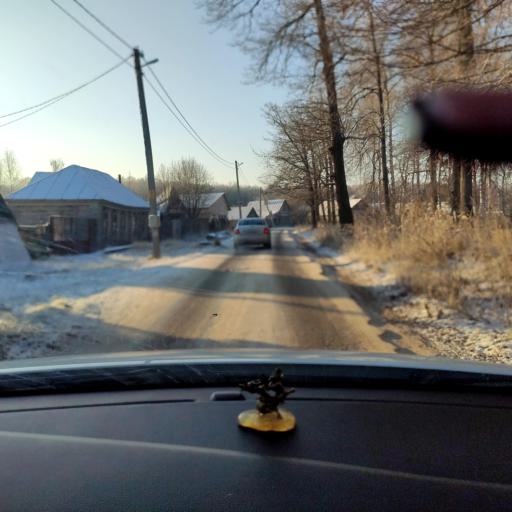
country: RU
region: Tatarstan
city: Stolbishchi
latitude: 55.6746
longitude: 49.1113
